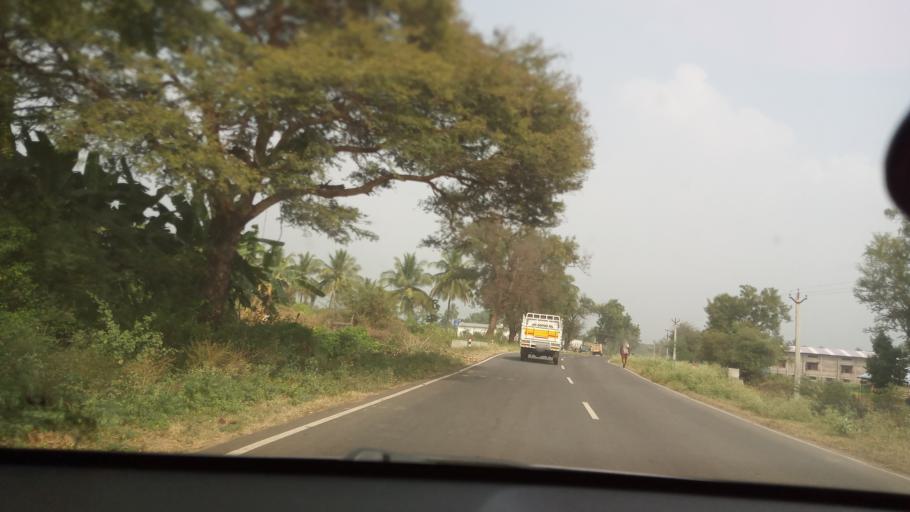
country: IN
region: Tamil Nadu
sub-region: Erode
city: Sathyamangalam
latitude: 11.5374
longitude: 77.1385
